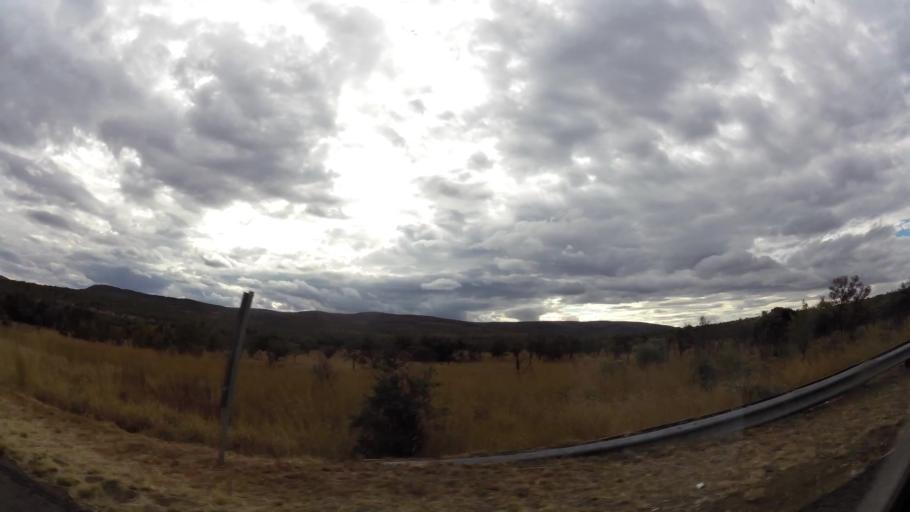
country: ZA
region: Limpopo
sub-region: Waterberg District Municipality
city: Modimolle
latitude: -24.6365
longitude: 28.6036
